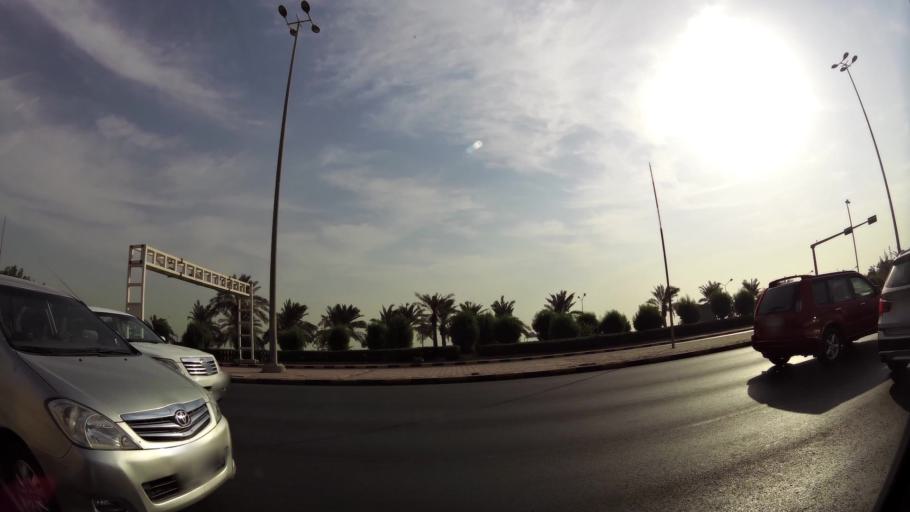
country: KW
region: Muhafazat Hawalli
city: Salwa
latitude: 29.2806
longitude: 48.0876
